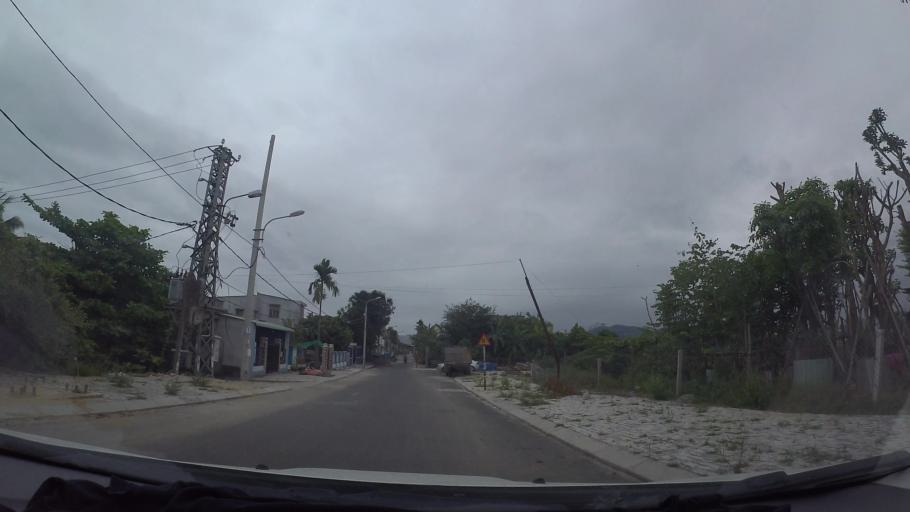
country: VN
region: Da Nang
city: Lien Chieu
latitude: 16.1078
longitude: 108.1284
